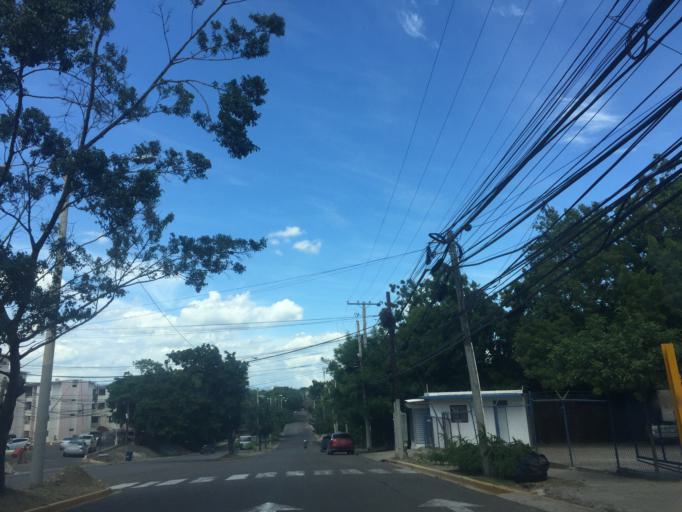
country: DO
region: Santiago
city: Santiago de los Caballeros
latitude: 19.4353
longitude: -70.6863
